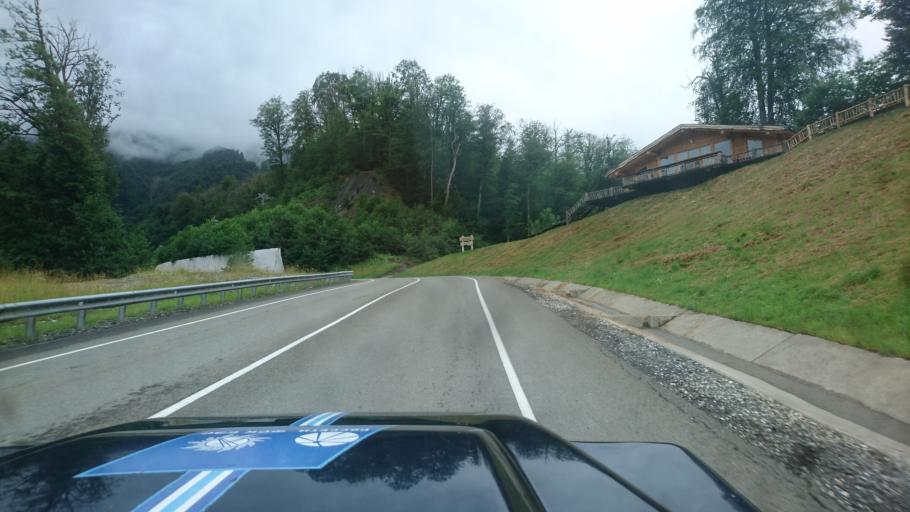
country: RU
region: Krasnodarskiy
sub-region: Sochi City
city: Krasnaya Polyana
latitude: 43.6668
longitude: 40.3001
